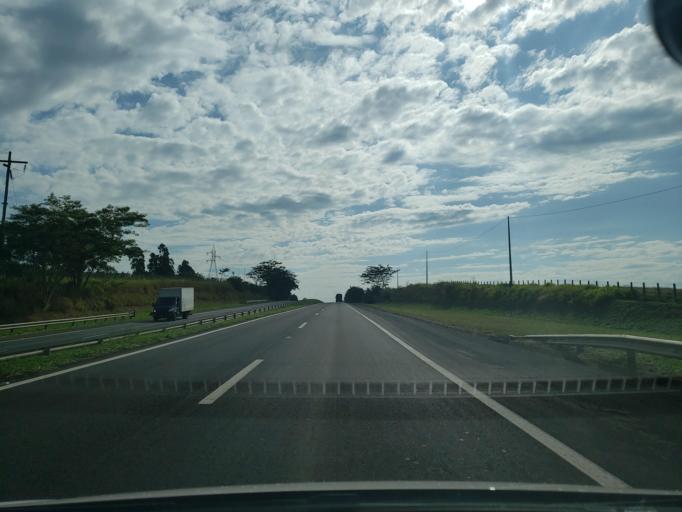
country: BR
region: Sao Paulo
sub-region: Lins
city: Lins
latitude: -21.6767
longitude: -49.7741
